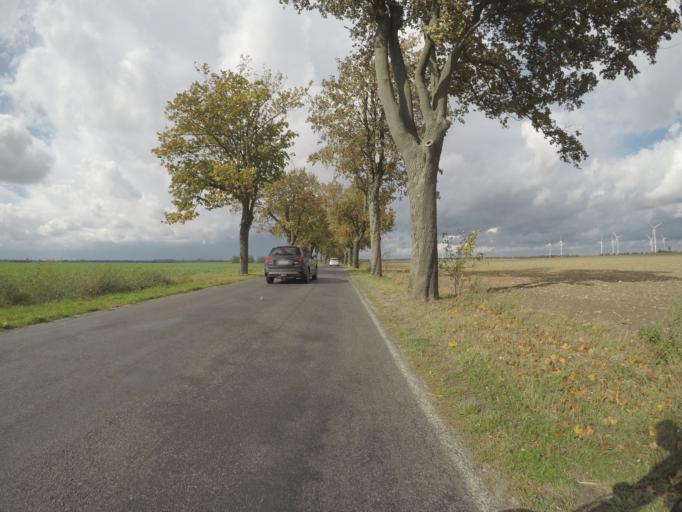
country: DE
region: Brandenburg
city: Altlandsberg
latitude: 52.5880
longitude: 13.7818
